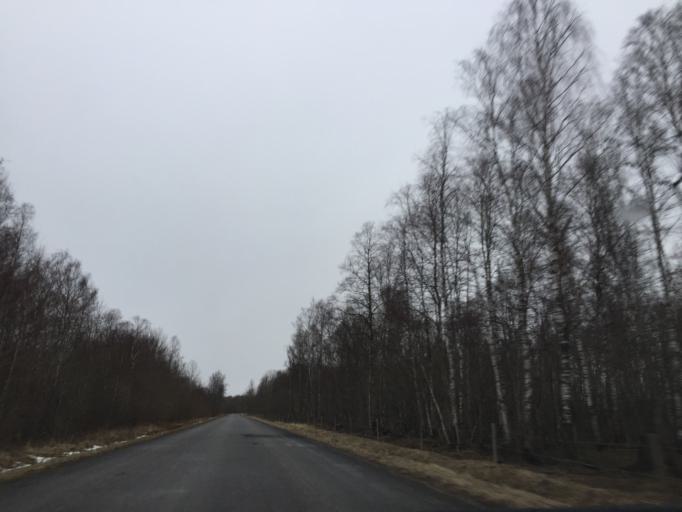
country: EE
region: Laeaene
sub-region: Lihula vald
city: Lihula
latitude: 58.6291
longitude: 23.6330
